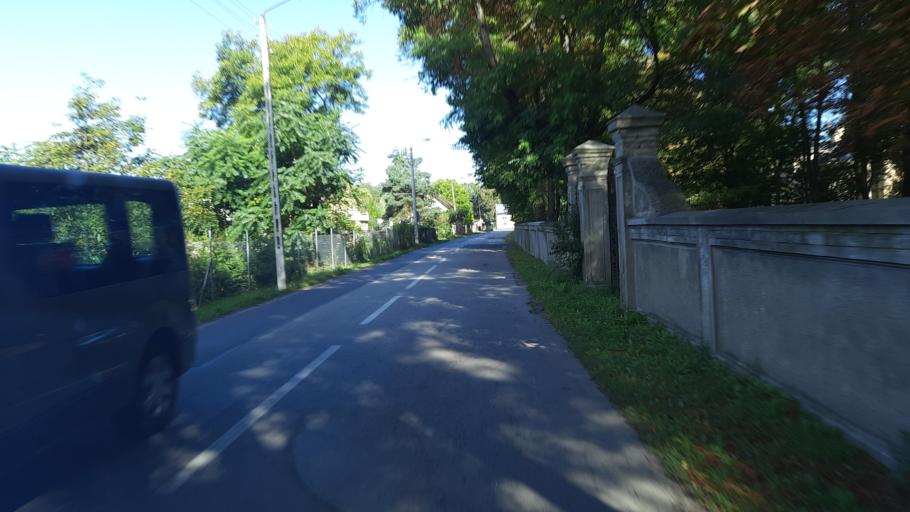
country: PL
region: Lower Silesian Voivodeship
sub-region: Powiat wroclawski
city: Dlugoleka
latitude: 51.1928
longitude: 17.1842
